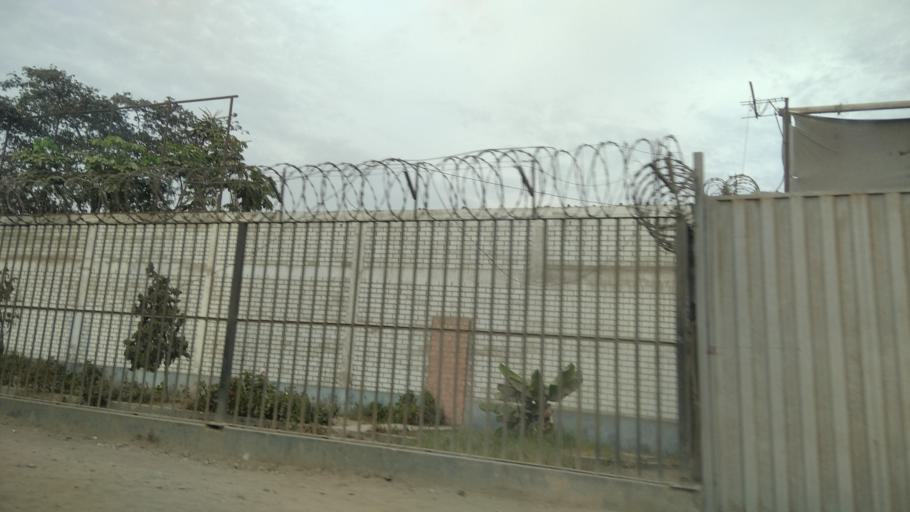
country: PE
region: Lima
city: Lima
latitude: -12.0182
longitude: -76.9987
